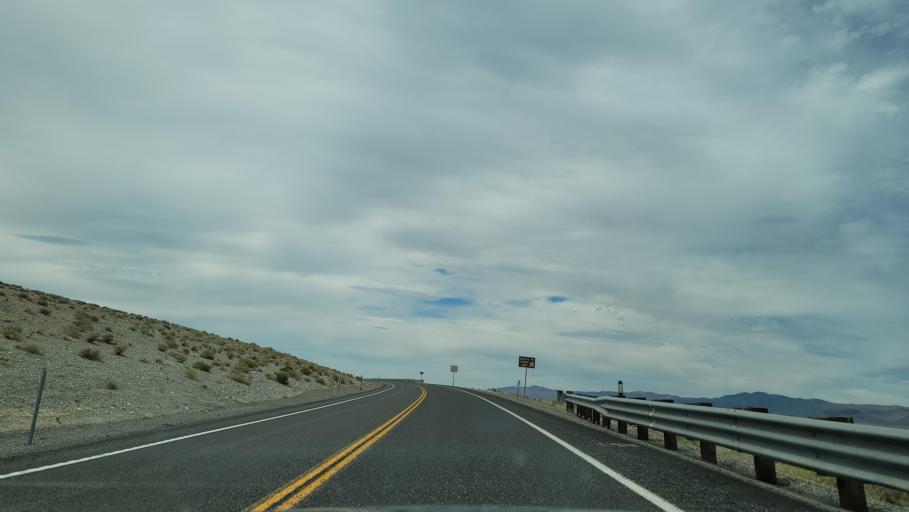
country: US
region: Nevada
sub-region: Mineral County
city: Hawthorne
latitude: 38.5955
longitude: -118.7074
